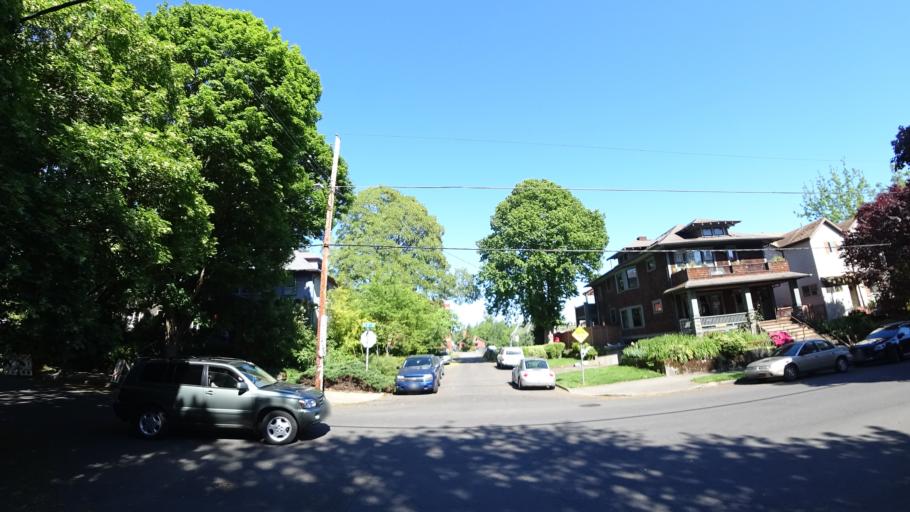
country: US
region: Oregon
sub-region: Multnomah County
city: Portland
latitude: 45.5243
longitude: -122.6416
